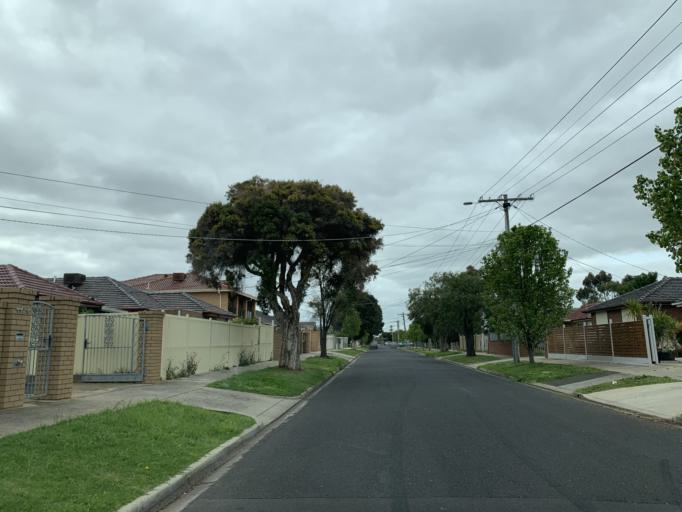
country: AU
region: Victoria
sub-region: Brimbank
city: St Albans
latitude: -37.7403
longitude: 144.8083
